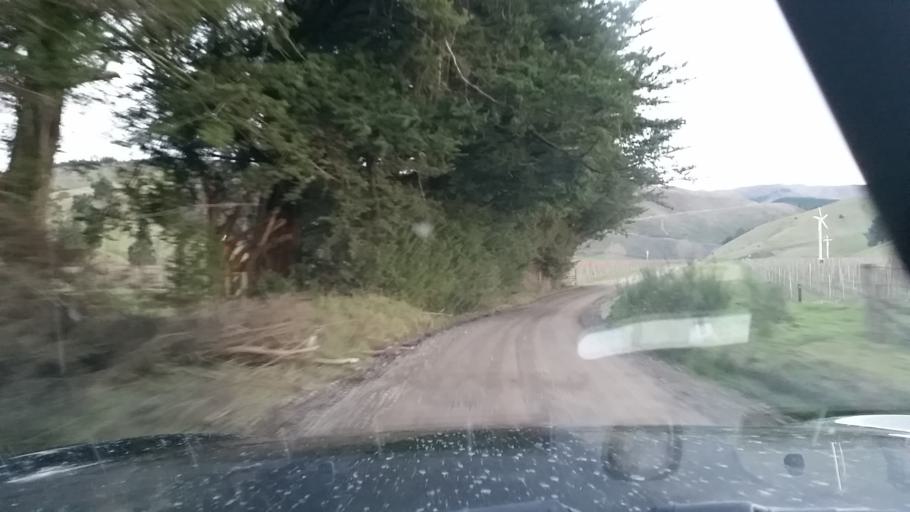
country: NZ
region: Nelson
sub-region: Nelson City
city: Nelson
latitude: -41.5821
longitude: 173.5090
